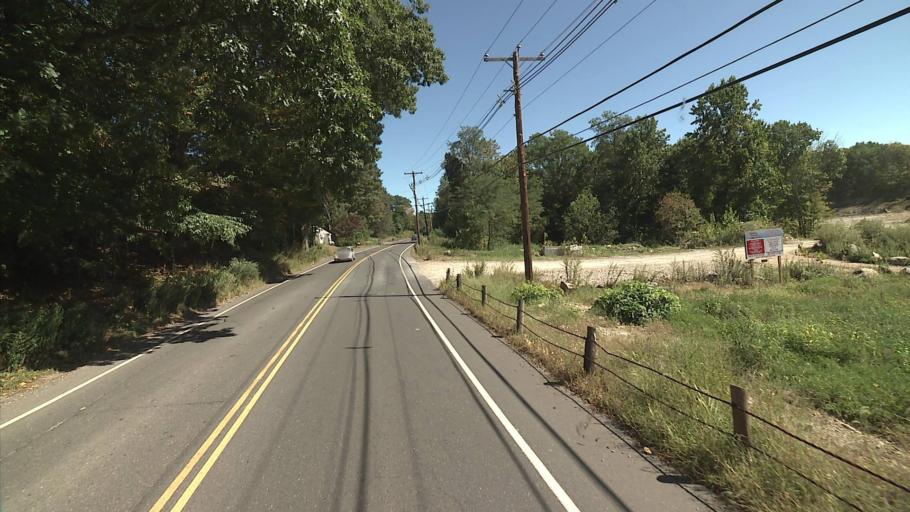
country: US
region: Connecticut
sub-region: New Haven County
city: Prospect
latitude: 41.5049
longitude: -73.0160
